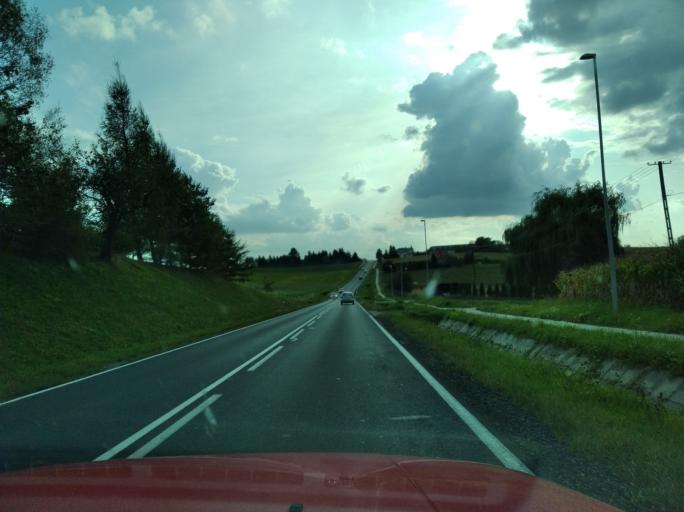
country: PL
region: Subcarpathian Voivodeship
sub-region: Powiat jaroslawski
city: Pawlosiow
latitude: 49.9907
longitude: 22.6628
